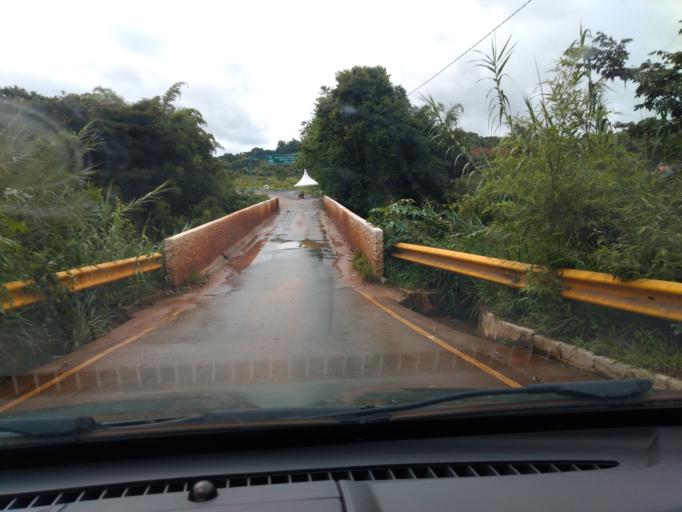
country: BR
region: Minas Gerais
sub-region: Lavras
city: Lavras
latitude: -21.5063
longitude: -44.9156
